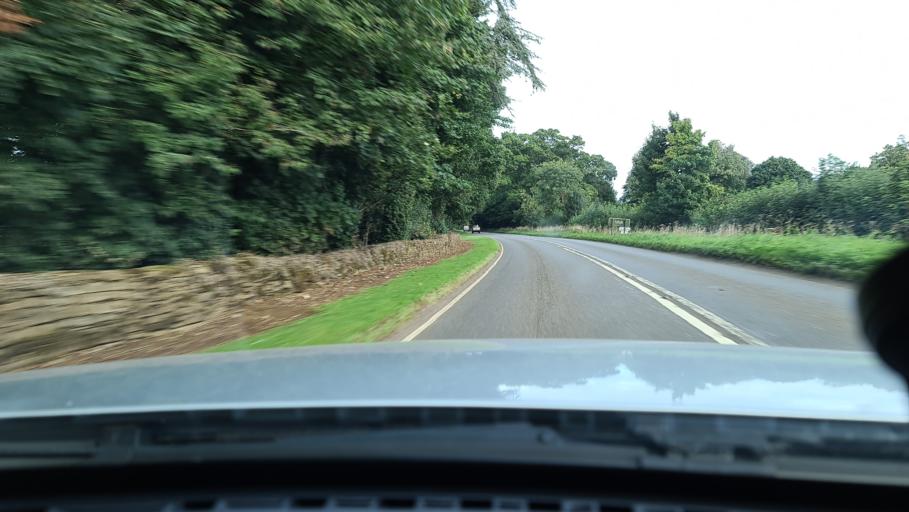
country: GB
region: England
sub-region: Oxfordshire
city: Hanwell
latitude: 52.1088
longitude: -1.4547
